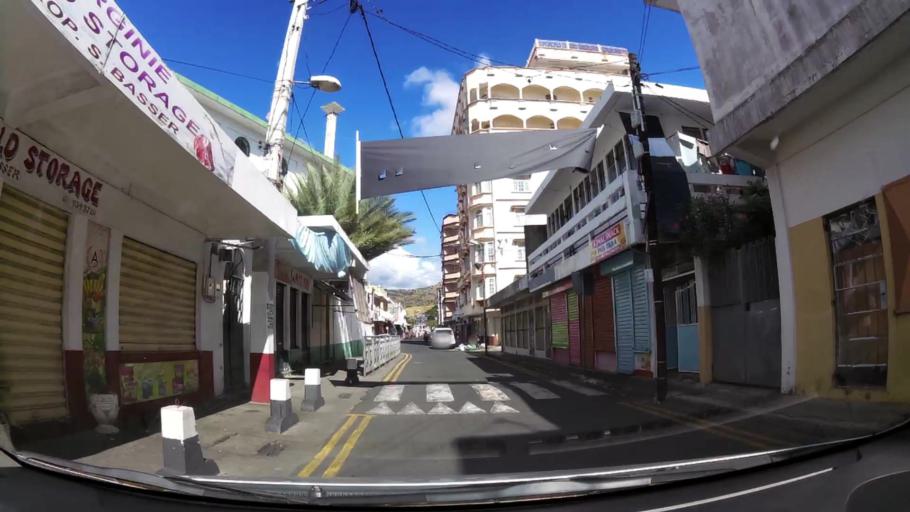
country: MU
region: Port Louis
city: Port Louis
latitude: -20.1616
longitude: 57.5164
